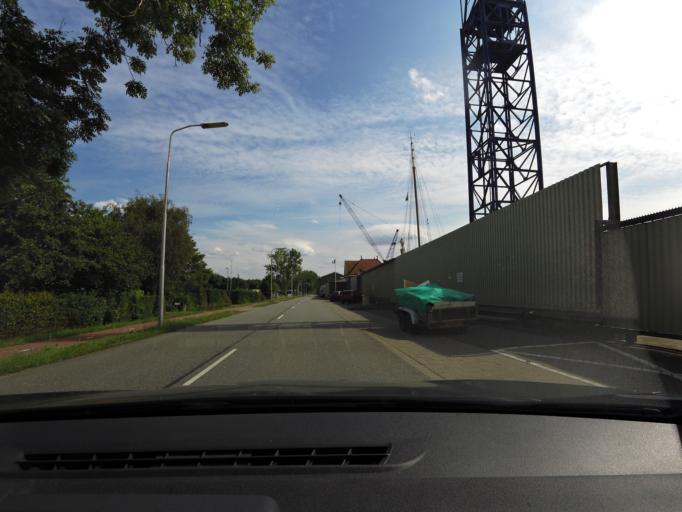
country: NL
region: South Holland
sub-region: Gemeente Delft
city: Delft
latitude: 51.9808
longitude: 4.3803
